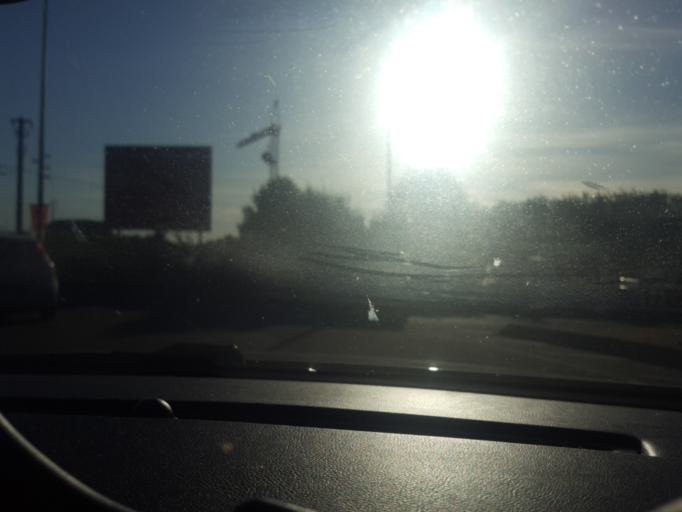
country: PT
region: Viseu
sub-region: Nelas
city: Nelas
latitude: 40.5390
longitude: -7.8565
